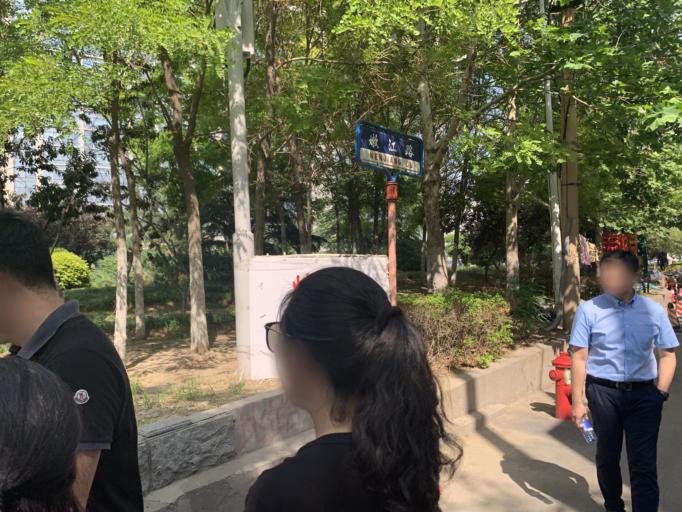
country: CN
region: Tianjin Shi
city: Quanyechang
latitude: 39.1285
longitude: 117.1896
